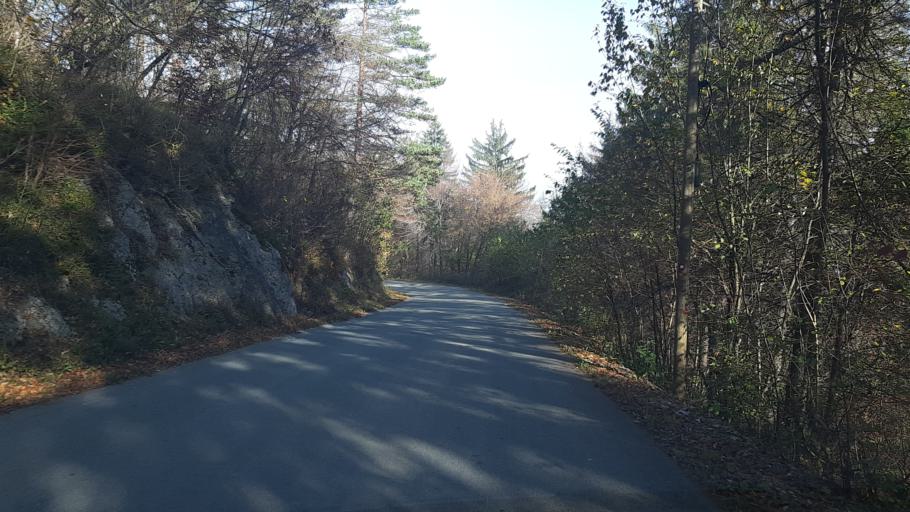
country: SI
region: Borovnica
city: Borovnica
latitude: 45.9068
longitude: 14.3638
